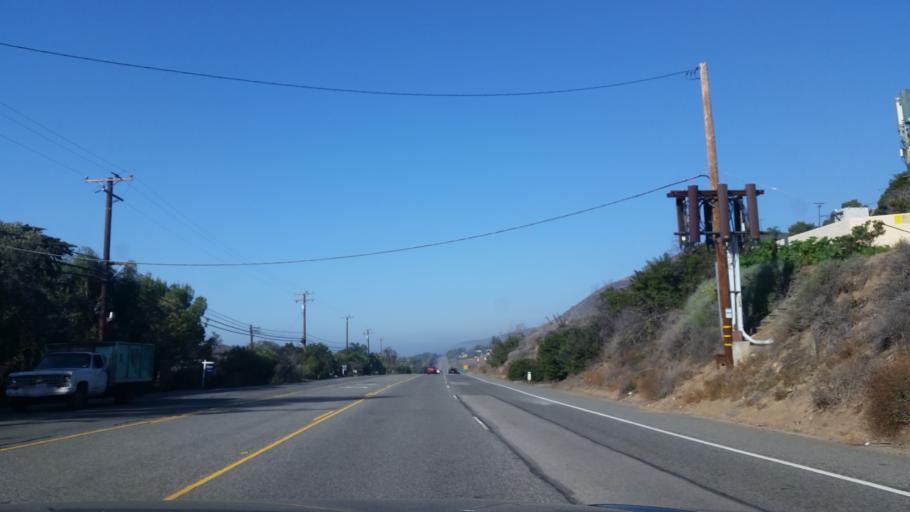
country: US
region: California
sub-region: Los Angeles County
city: Malibu
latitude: 34.0407
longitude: -118.8885
